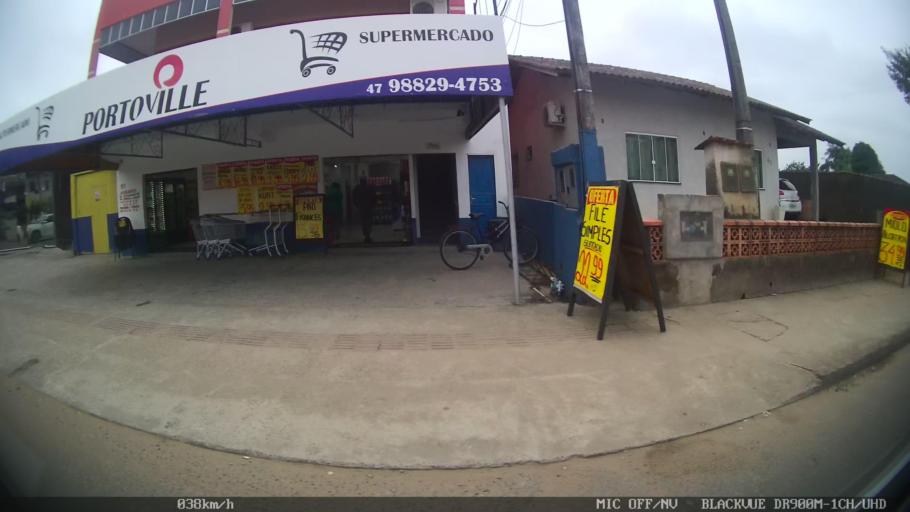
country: BR
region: Santa Catarina
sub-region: Joinville
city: Joinville
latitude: -26.3392
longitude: -48.8243
